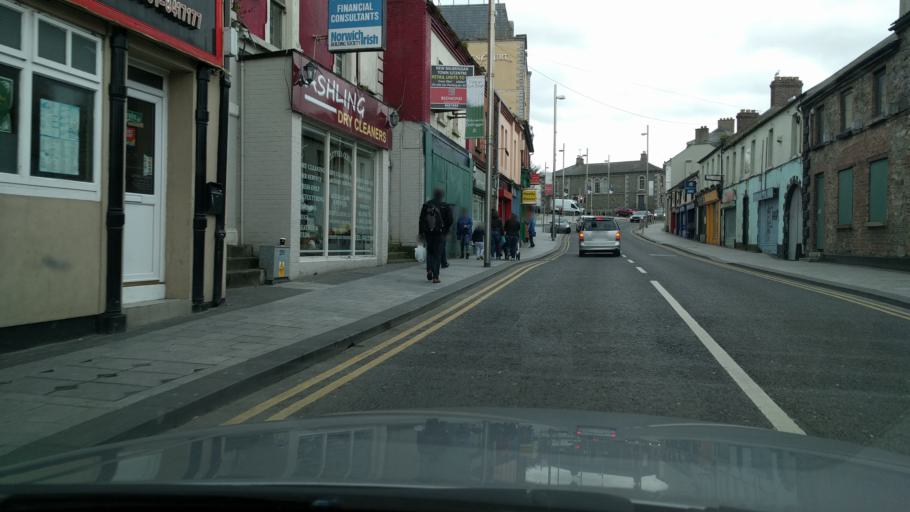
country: IE
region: Leinster
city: Balbriggan
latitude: 53.6095
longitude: -6.1834
